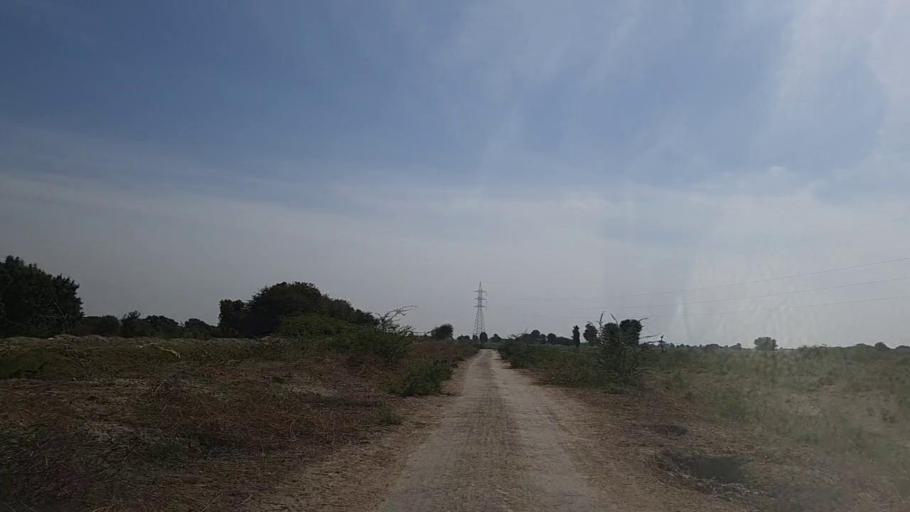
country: PK
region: Sindh
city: Samaro
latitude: 25.2088
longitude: 69.4564
